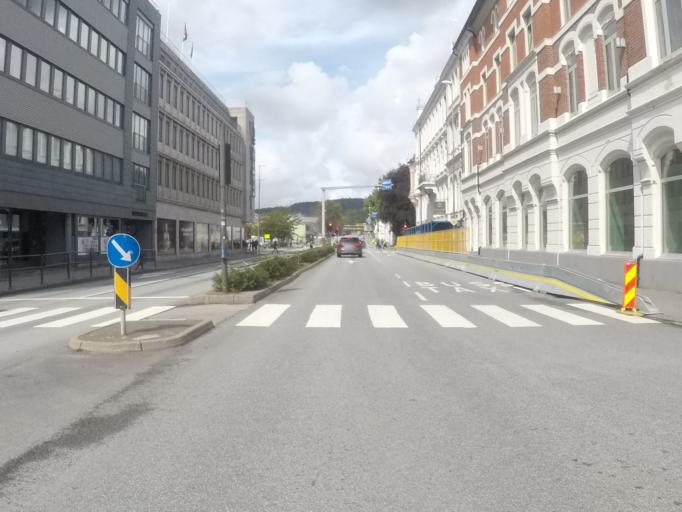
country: NO
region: Vest-Agder
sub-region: Kristiansand
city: Kristiansand
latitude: 58.1438
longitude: 7.9931
